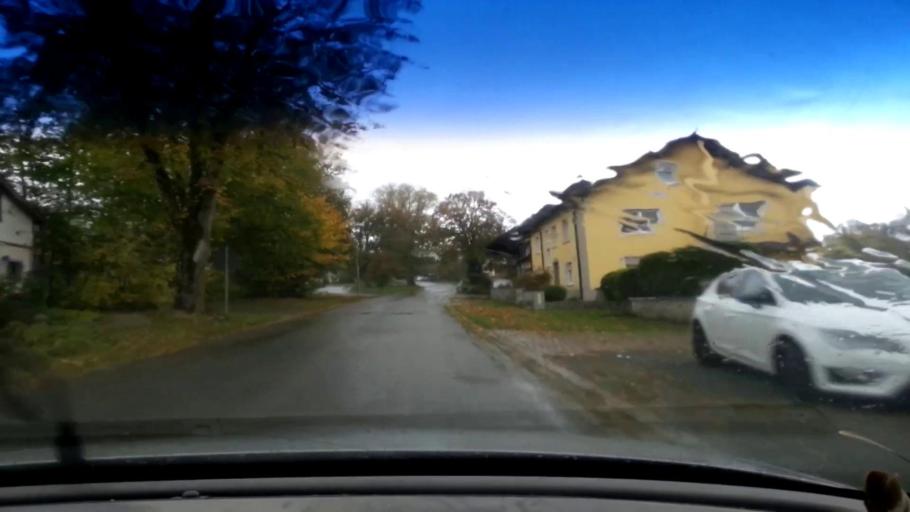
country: DE
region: Bavaria
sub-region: Upper Franconia
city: Stadelhofen
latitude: 50.0418
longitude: 11.2058
